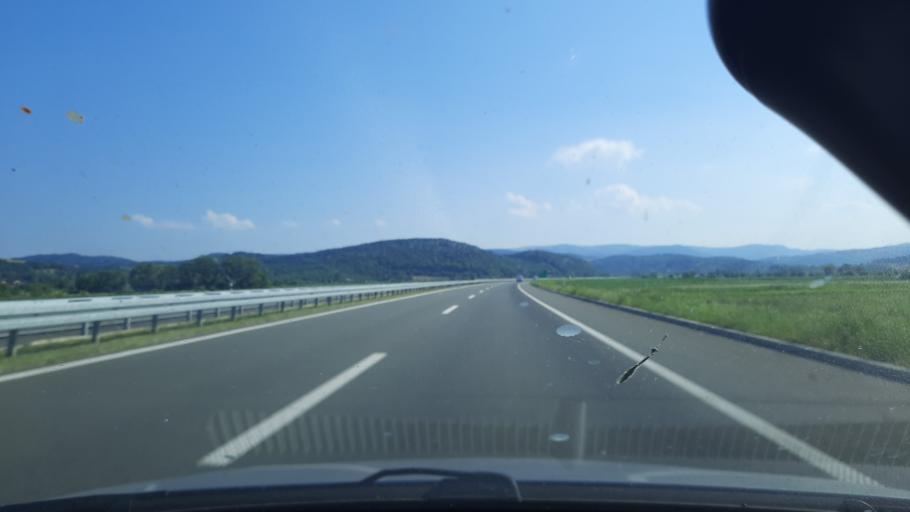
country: RS
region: Central Serbia
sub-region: Kolubarski Okrug
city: Ljig
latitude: 44.2537
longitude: 20.2700
